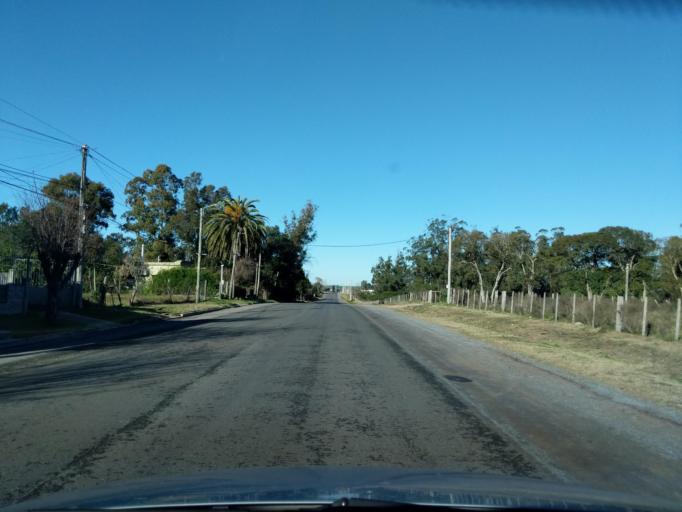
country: UY
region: Florida
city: Florida
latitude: -34.0938
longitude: -56.2396
